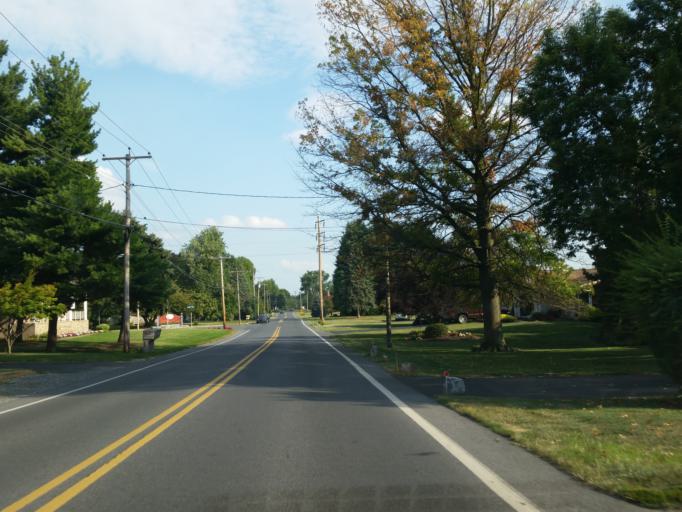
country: US
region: Pennsylvania
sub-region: Lebanon County
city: Palmyra
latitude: 40.3012
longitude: -76.5793
